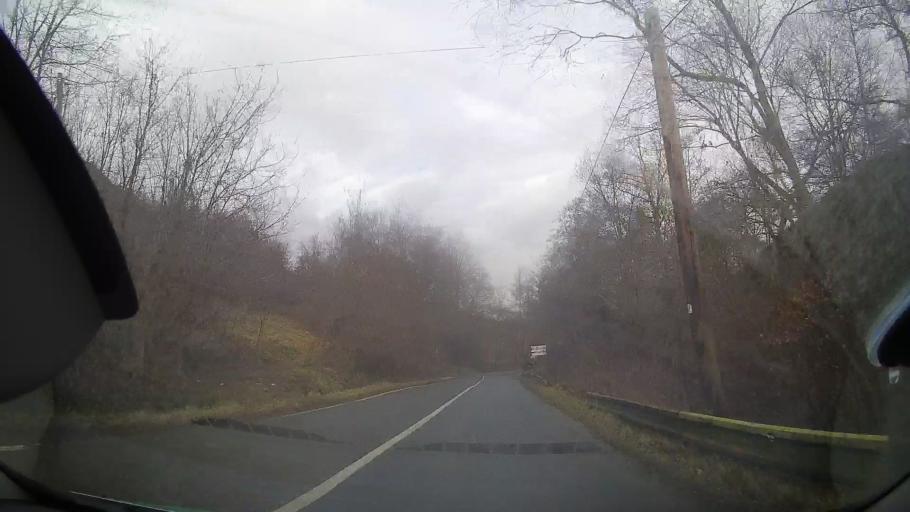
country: RO
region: Alba
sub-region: Comuna Ocolis
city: Ocolis
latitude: 46.4535
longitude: 23.4675
